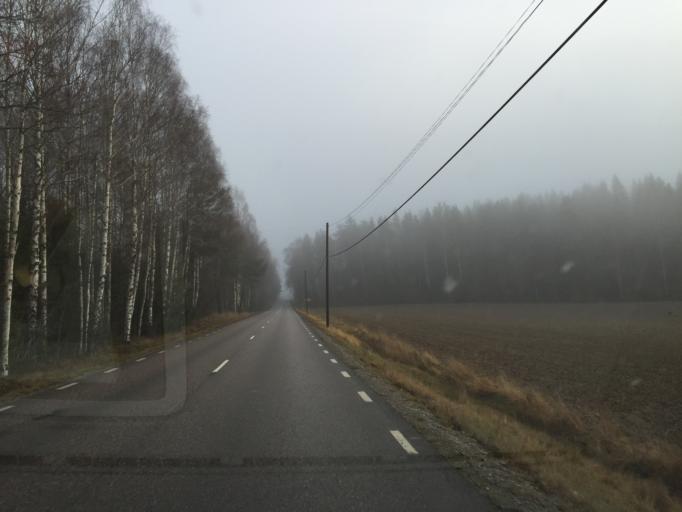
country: SE
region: Stockholm
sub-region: Botkyrka Kommun
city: Varsta
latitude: 59.1096
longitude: 17.8696
